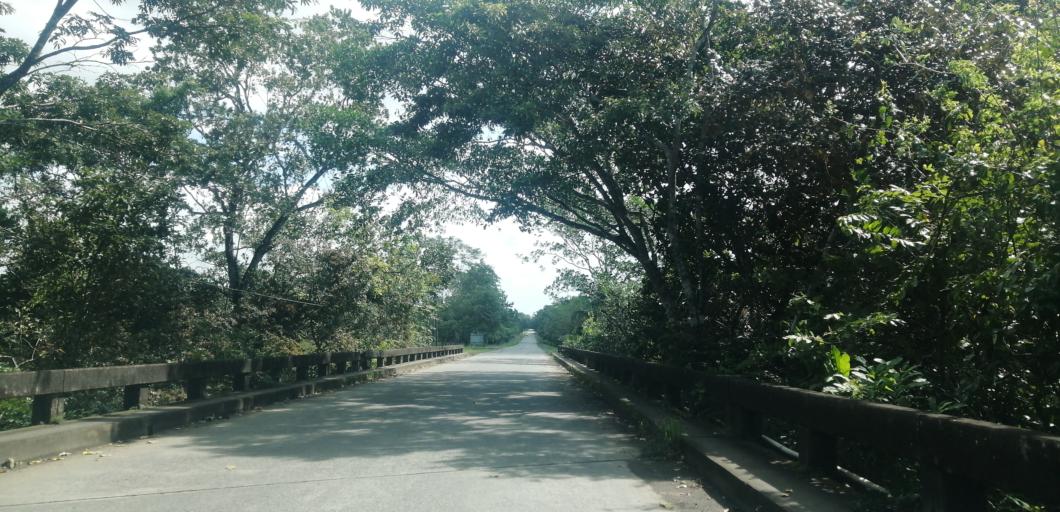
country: PA
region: Panama
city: Canita
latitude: 9.2213
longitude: -78.8880
